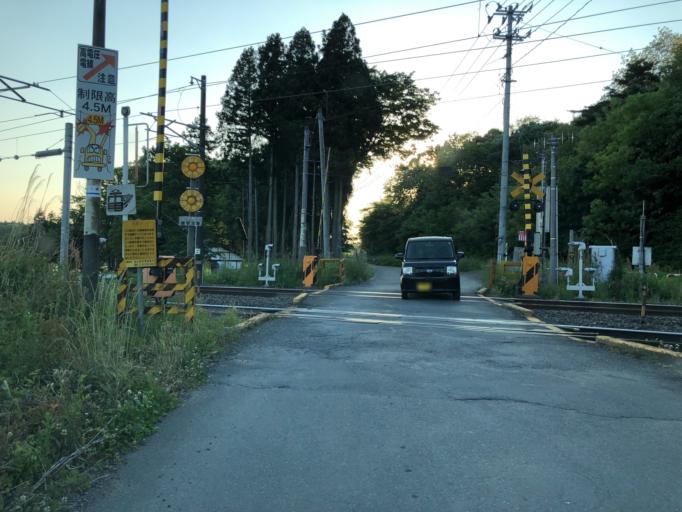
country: JP
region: Fukushima
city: Sukagawa
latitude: 37.1854
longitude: 140.3098
